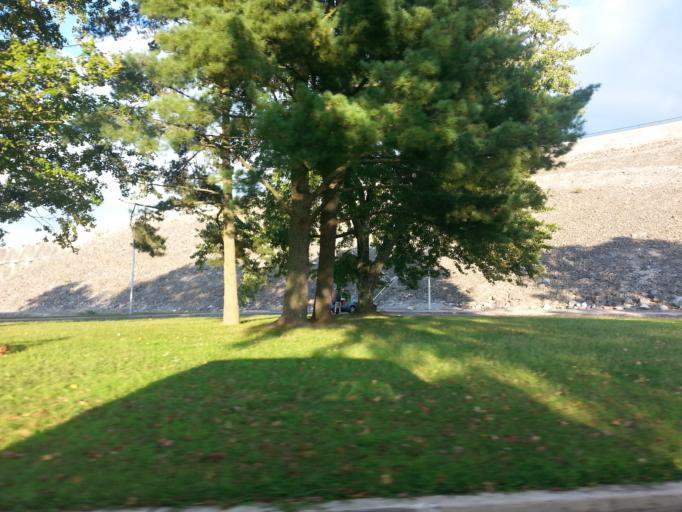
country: US
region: Tennessee
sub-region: Jefferson County
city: Jefferson City
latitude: 36.1648
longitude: -83.5010
